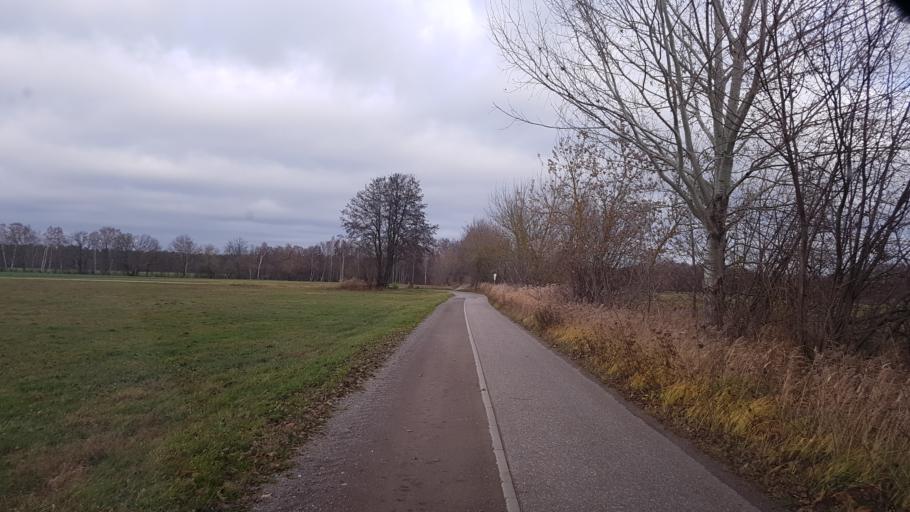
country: DE
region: Brandenburg
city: Ruckersdorf
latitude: 51.5956
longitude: 13.6251
